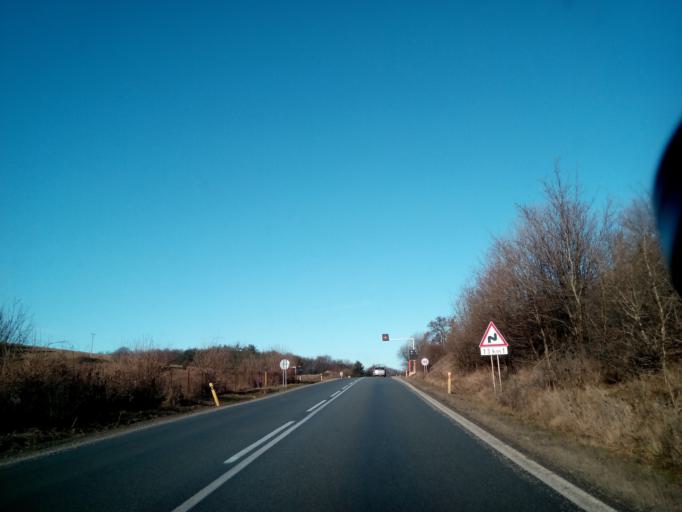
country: SK
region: Kosicky
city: Roznava
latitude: 48.6169
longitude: 20.6309
